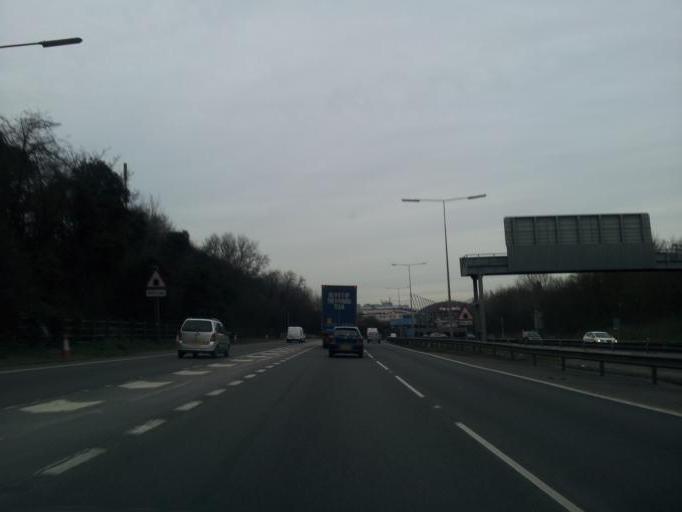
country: GB
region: England
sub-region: Hertfordshire
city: Hatfield
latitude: 51.7571
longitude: -0.2444
